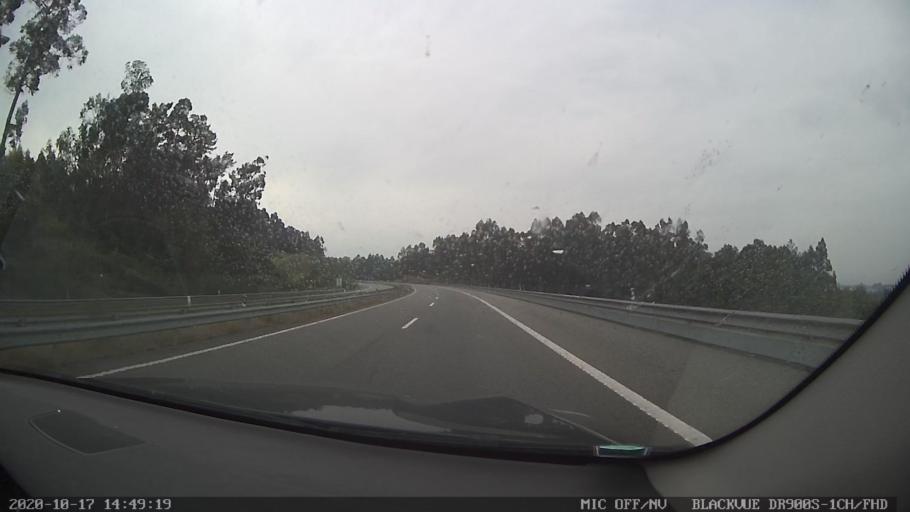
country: PT
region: Braga
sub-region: Barcelos
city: Galegos
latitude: 41.5331
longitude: -8.5616
